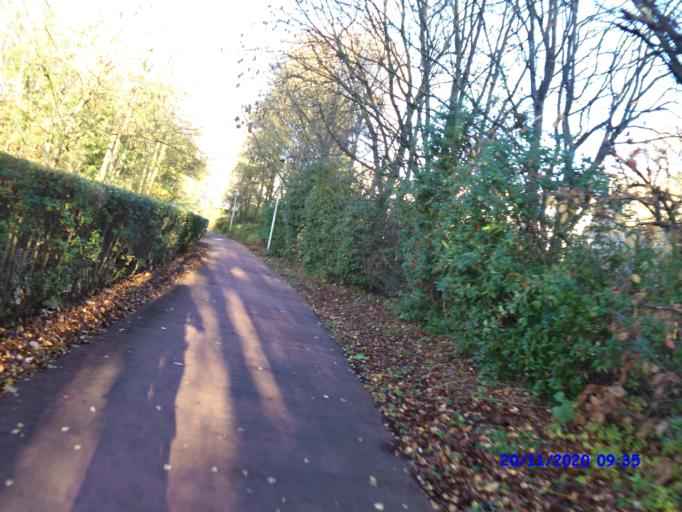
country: BE
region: Flanders
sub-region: Provincie Vlaams-Brabant
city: Kraainem
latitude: 50.8506
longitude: 4.4263
